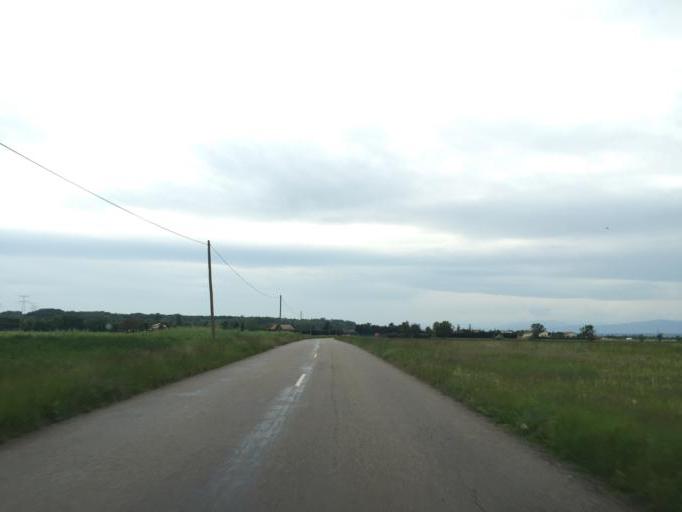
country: FR
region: Rhone-Alpes
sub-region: Departement de la Drome
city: Montelier
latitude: 44.9155
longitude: 5.0418
